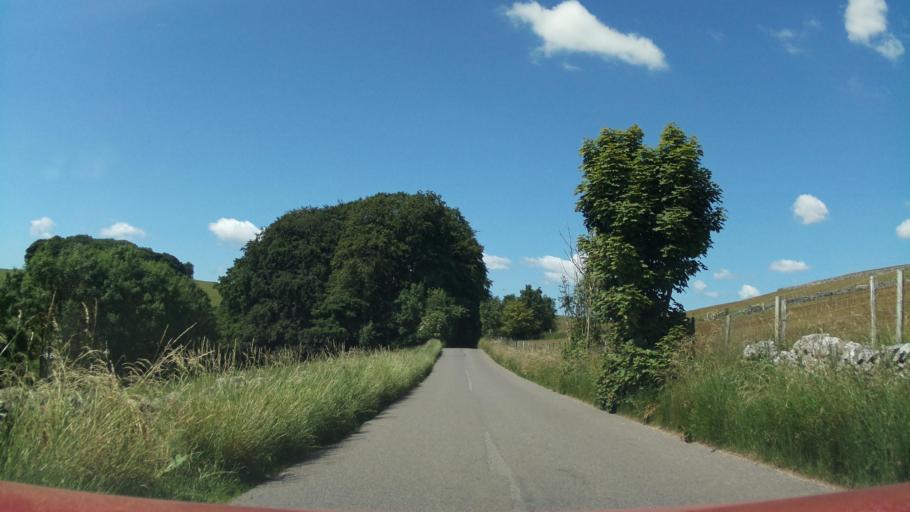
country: GB
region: England
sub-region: Derbyshire
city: Tideswell
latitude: 53.1879
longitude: -1.8191
